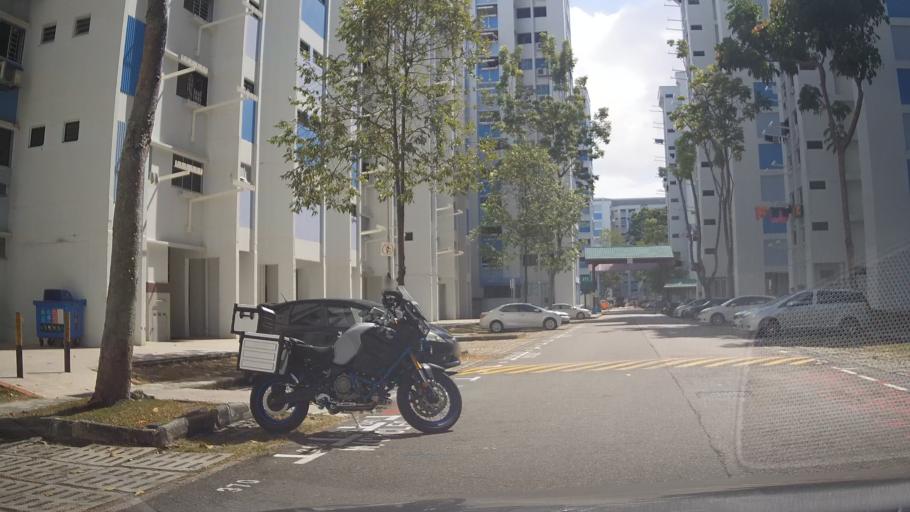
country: SG
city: Singapore
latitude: 1.3543
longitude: 103.9525
